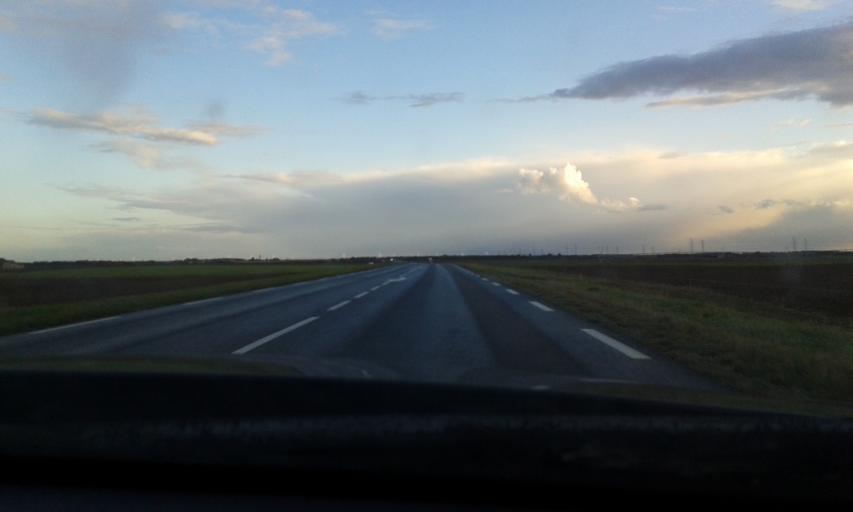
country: FR
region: Centre
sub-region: Departement d'Eure-et-Loir
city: Janville
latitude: 48.2431
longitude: 1.7770
